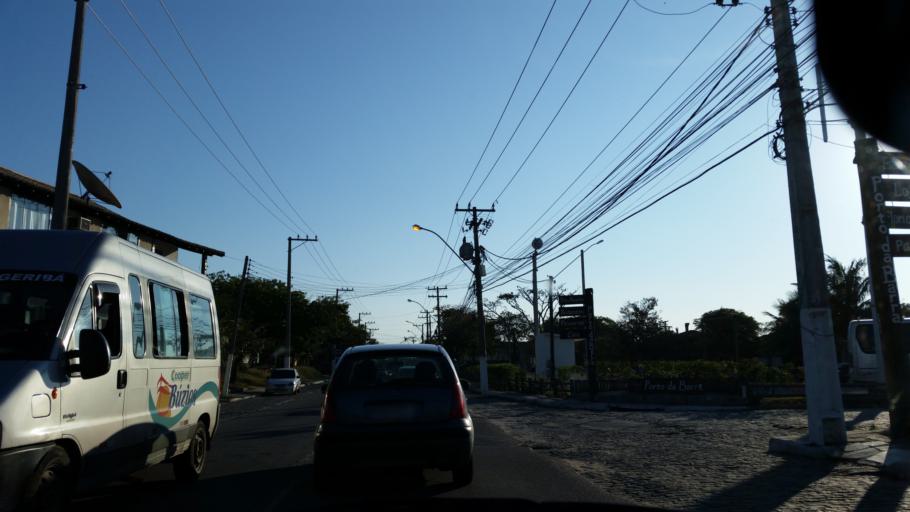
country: BR
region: Rio de Janeiro
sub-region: Armacao De Buzios
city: Armacao de Buzios
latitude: -22.7698
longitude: -41.9105
